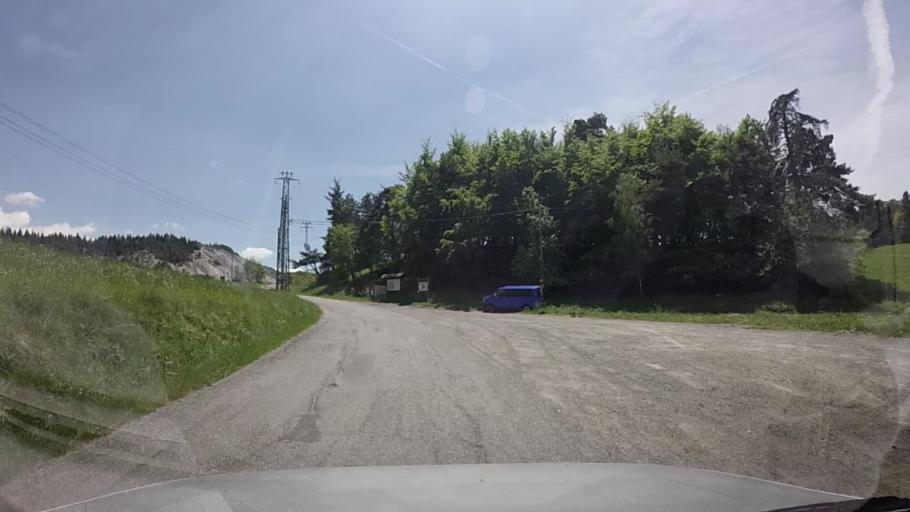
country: FR
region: Provence-Alpes-Cote d'Azur
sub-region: Departement des Alpes-de-Haute-Provence
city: Seyne-les-Alpes
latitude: 44.3275
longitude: 6.3276
